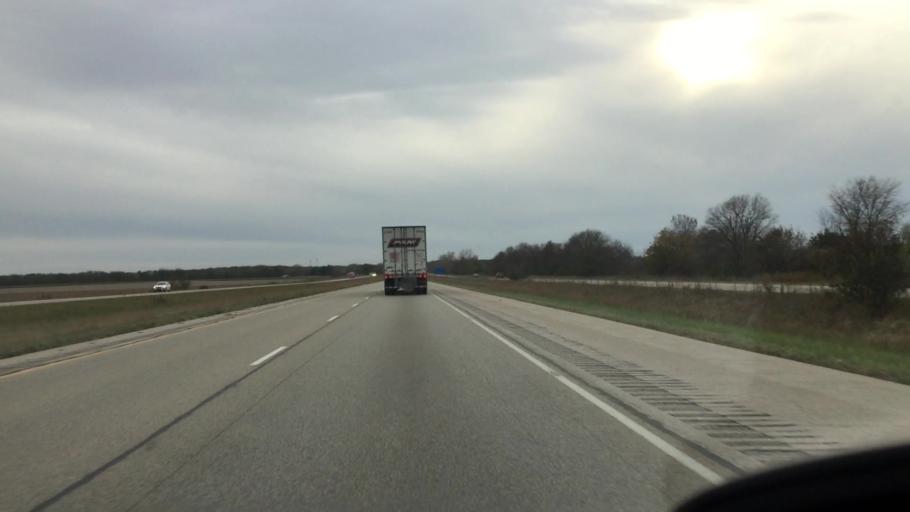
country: US
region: Illinois
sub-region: McLean County
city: Twin Grove
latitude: 40.3884
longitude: -89.0827
